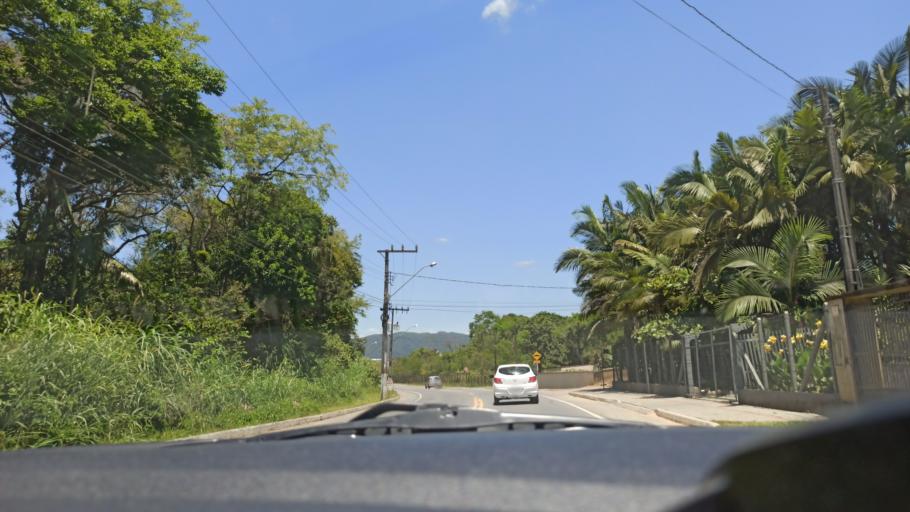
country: BR
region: Santa Catarina
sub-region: Indaial
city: Indaial
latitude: -26.8851
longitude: -49.2406
